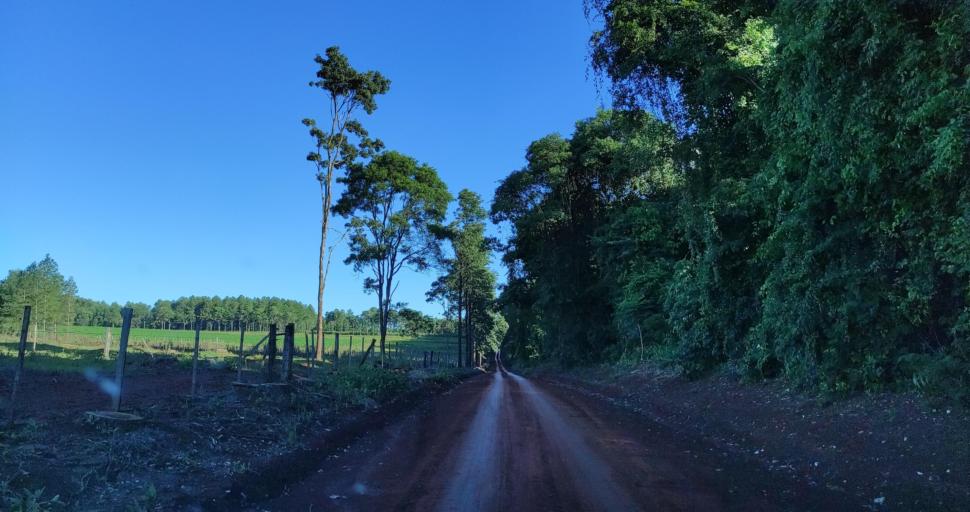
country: AR
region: Misiones
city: Puerto Rico
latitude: -26.8388
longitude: -55.0125
